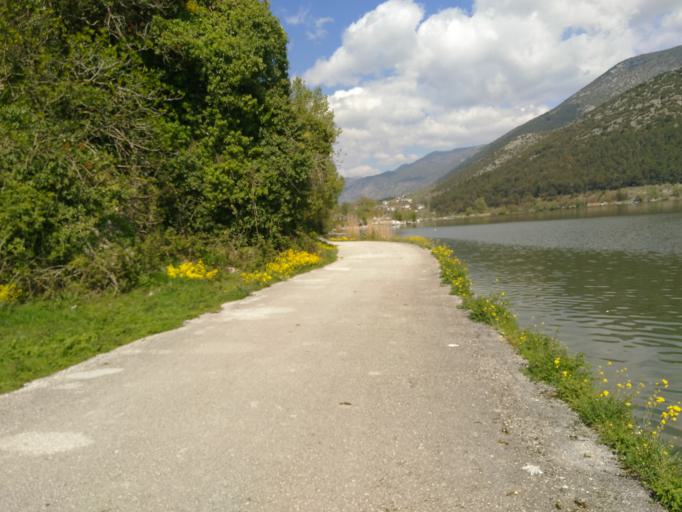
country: GR
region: Epirus
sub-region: Nomos Ioanninon
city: Ioannina
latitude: 39.6772
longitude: 20.8781
